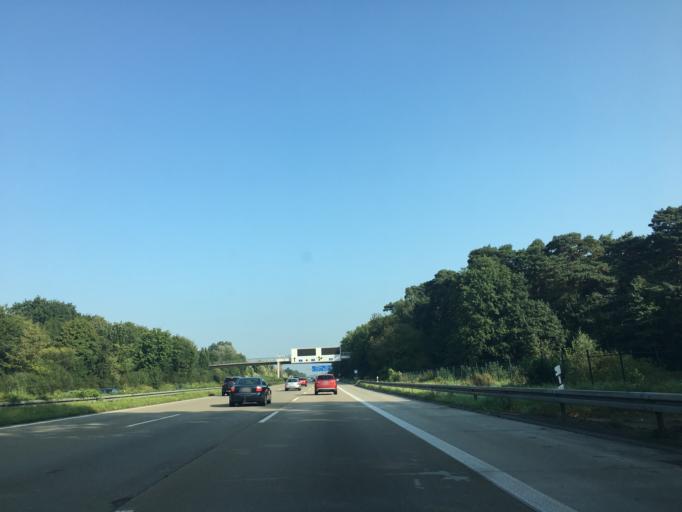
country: DE
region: North Rhine-Westphalia
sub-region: Regierungsbezirk Dusseldorf
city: Hilden
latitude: 51.1794
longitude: 6.9480
